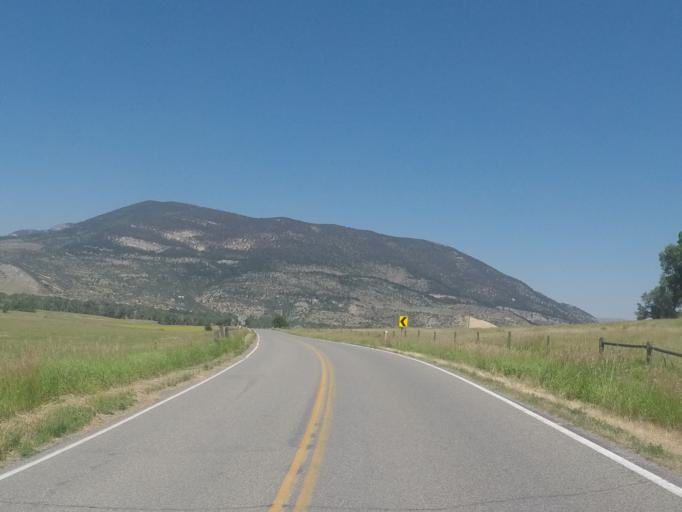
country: US
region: Montana
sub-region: Park County
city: Livingston
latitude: 45.5688
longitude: -110.5598
